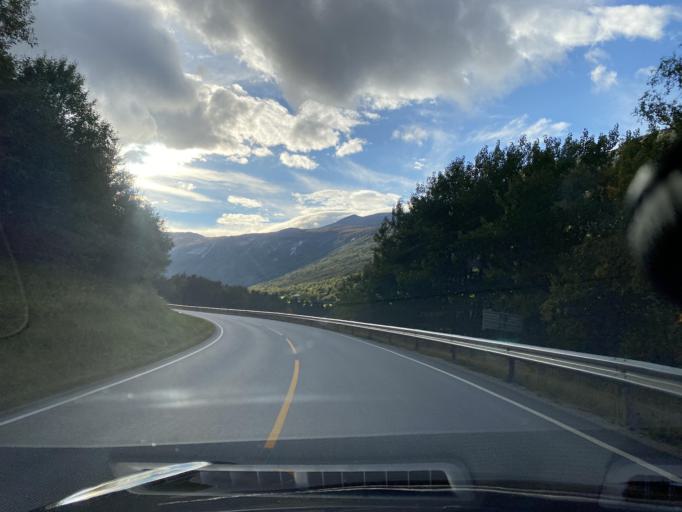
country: NO
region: Oppland
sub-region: Lom
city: Fossbergom
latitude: 61.8193
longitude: 8.5221
